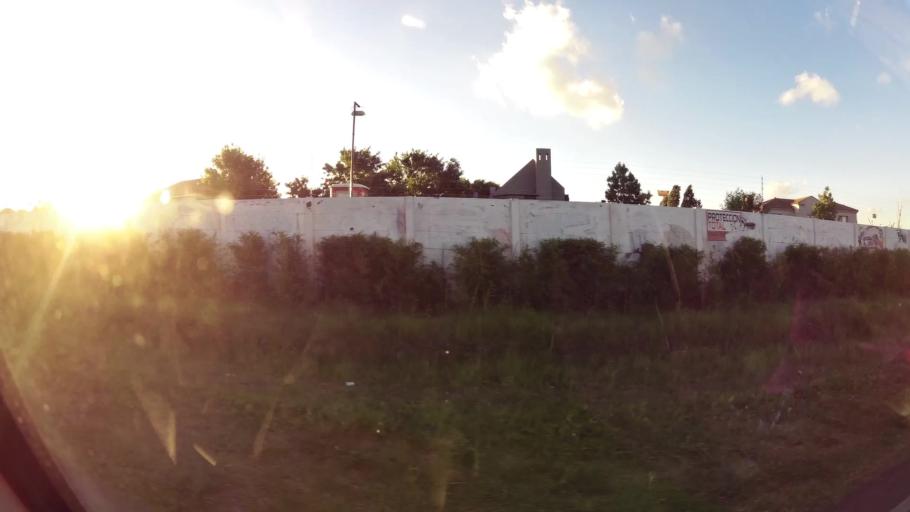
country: AR
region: Buenos Aires
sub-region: Partido de Quilmes
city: Quilmes
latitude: -34.7983
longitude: -58.1625
